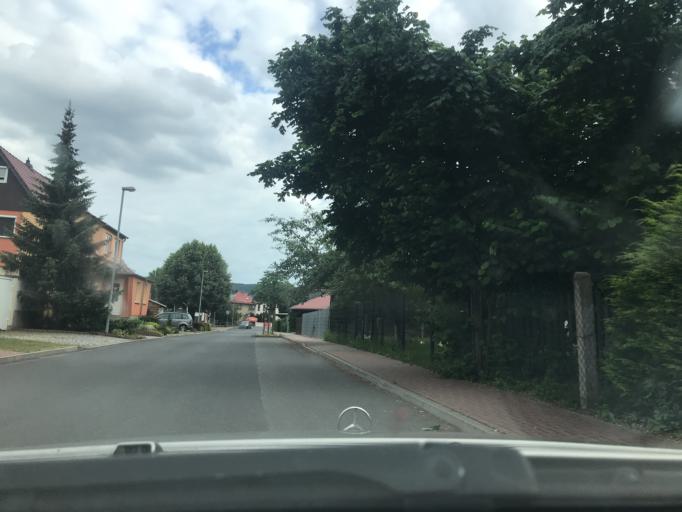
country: DE
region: Thuringia
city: Niederorschel
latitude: 51.3752
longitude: 10.4239
